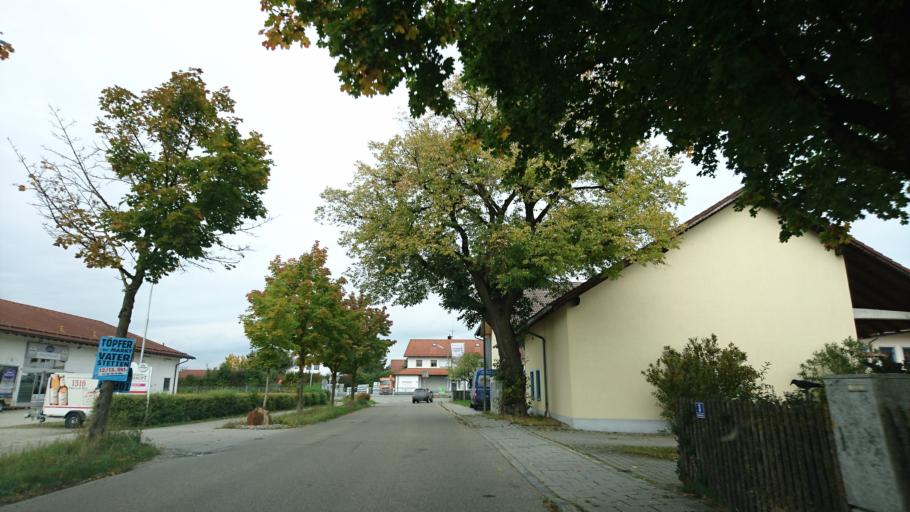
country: DE
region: Bavaria
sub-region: Upper Bavaria
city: Vaterstetten
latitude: 48.1135
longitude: 11.7943
